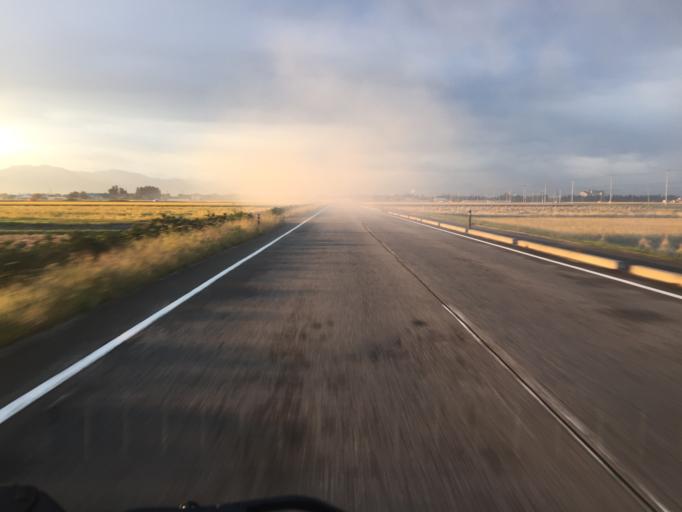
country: JP
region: Fukushima
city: Kitakata
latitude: 37.5437
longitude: 139.8988
